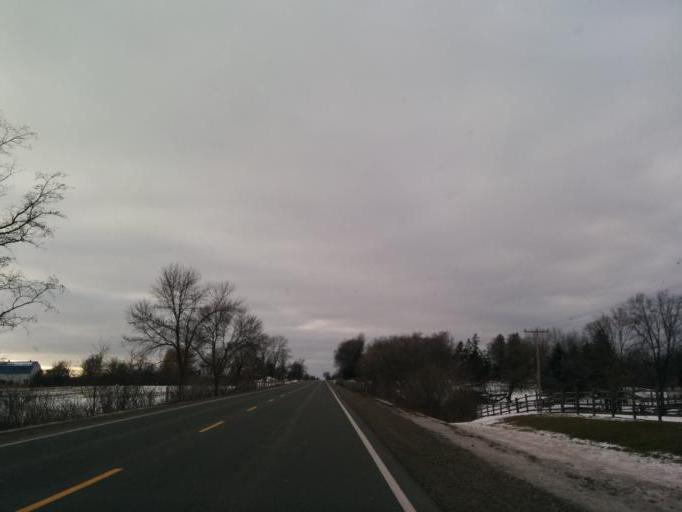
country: CA
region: Ontario
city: Ancaster
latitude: 42.9347
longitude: -79.9213
